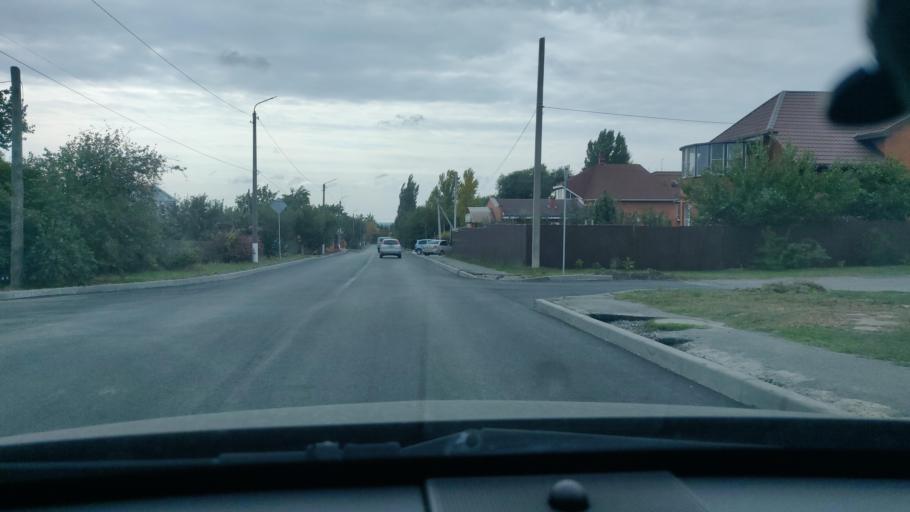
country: RU
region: Rostov
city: Ust'-Donetskiy
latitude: 47.6455
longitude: 40.8731
